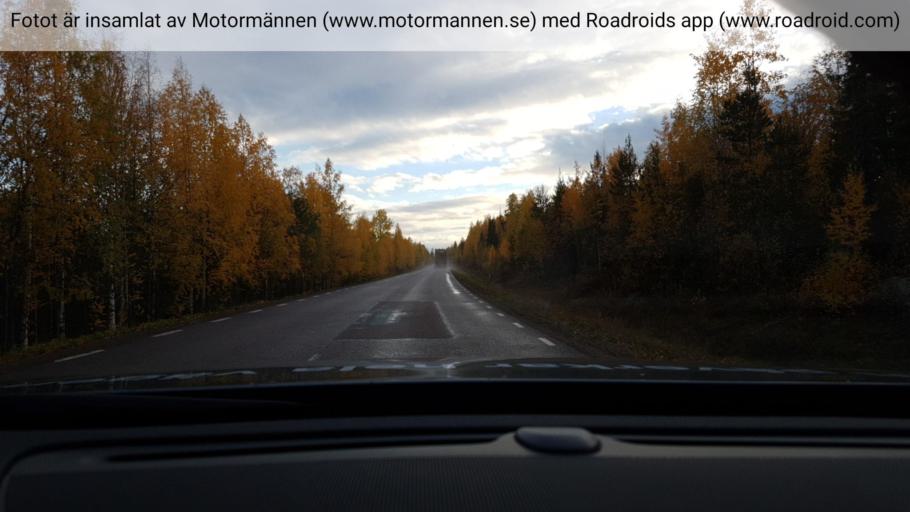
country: SE
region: Norrbotten
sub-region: Overkalix Kommun
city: OEverkalix
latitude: 66.8217
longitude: 22.7485
